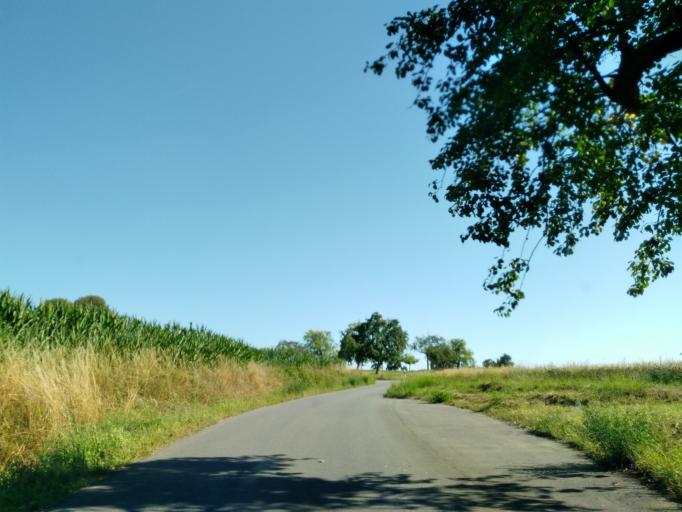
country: DE
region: Baden-Wuerttemberg
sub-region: Karlsruhe Region
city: Limbach
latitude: 49.4728
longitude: 9.2359
